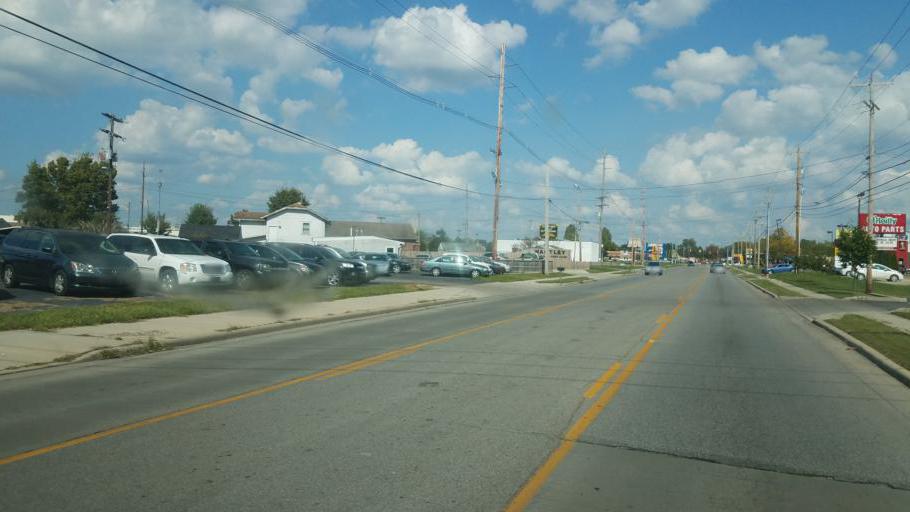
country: US
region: Ohio
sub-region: Franklin County
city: Grandview Heights
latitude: 39.9286
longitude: -83.0540
